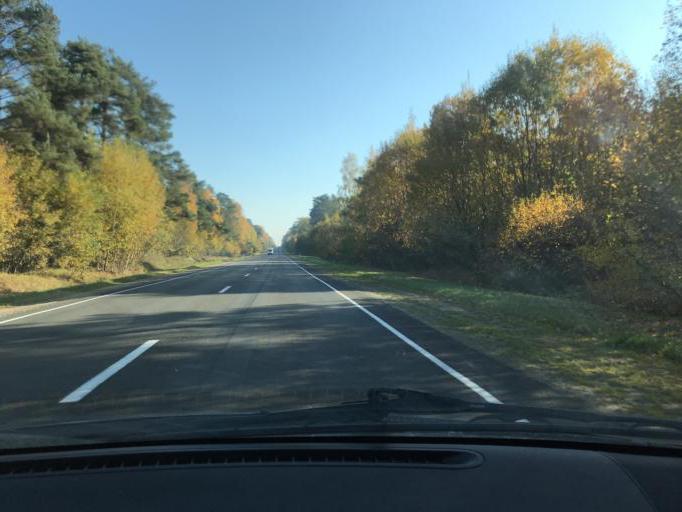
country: BY
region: Brest
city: Lyakhavichy
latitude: 52.9591
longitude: 26.3700
